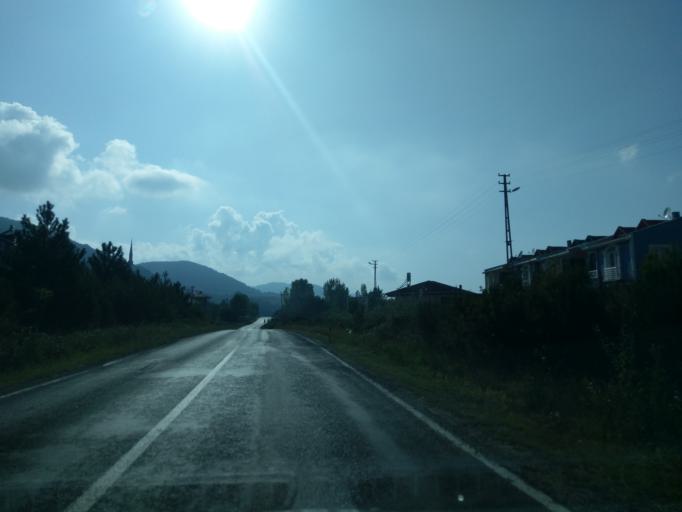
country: TR
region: Sinop
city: Yenikonak
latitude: 41.9432
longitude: 34.7291
